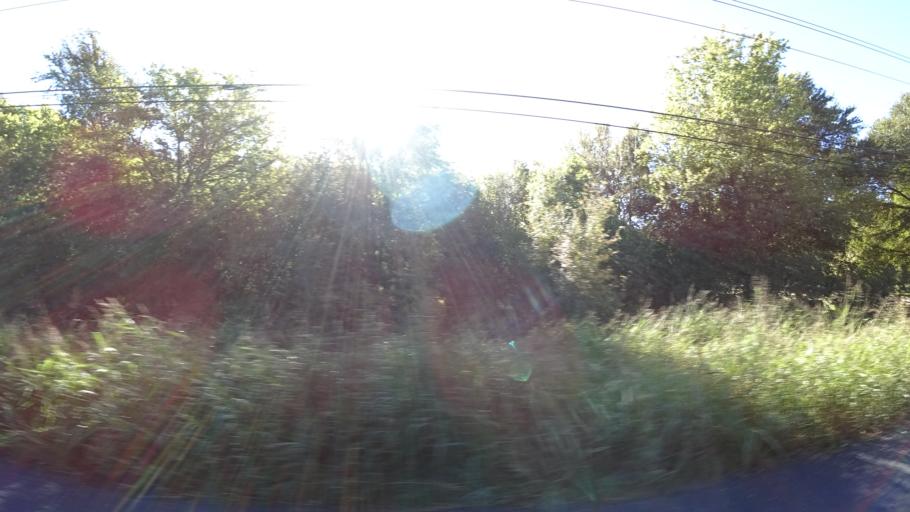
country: US
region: Texas
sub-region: Travis County
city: Austin
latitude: 30.2259
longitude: -97.6754
